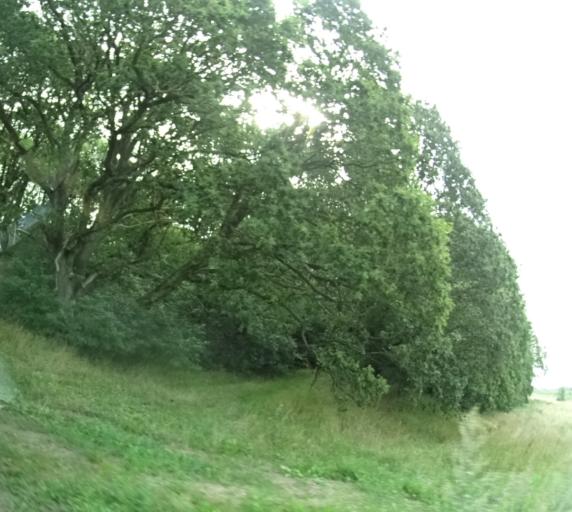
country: DK
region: Central Jutland
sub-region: Syddjurs Kommune
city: Ryomgard
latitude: 56.3487
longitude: 10.4986
